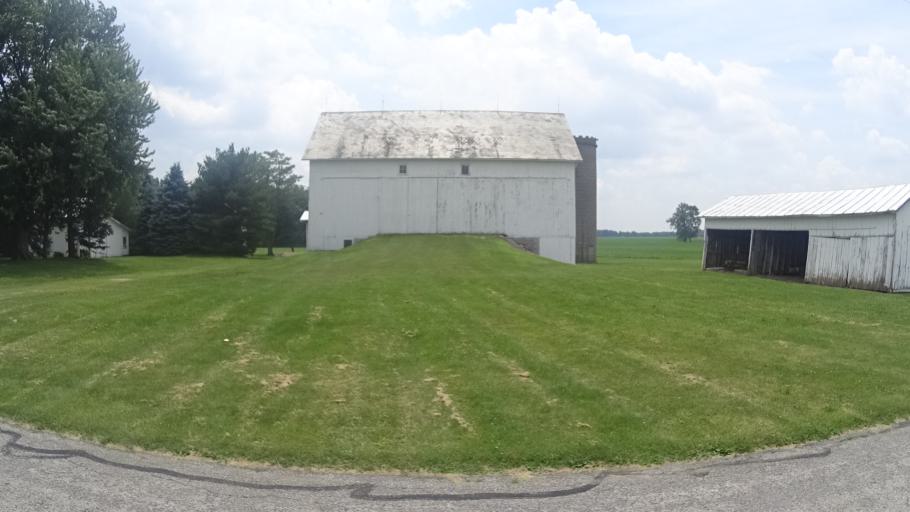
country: US
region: Ohio
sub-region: Erie County
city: Milan
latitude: 41.3109
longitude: -82.6445
